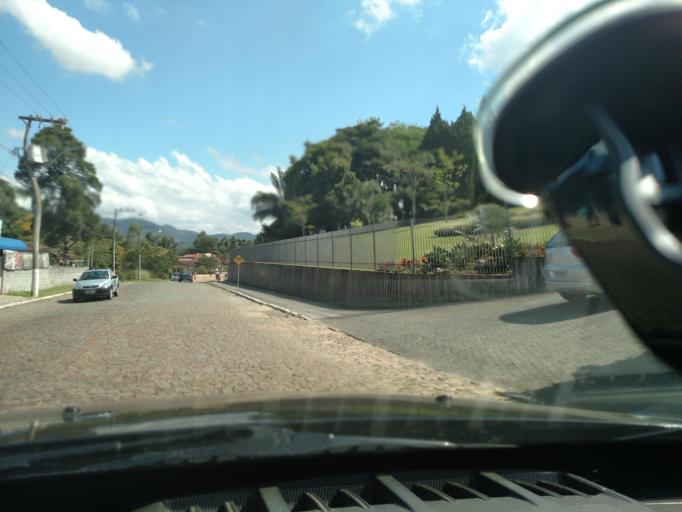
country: BR
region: Santa Catarina
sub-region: Indaial
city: Indaial
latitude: -26.8943
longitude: -49.2430
